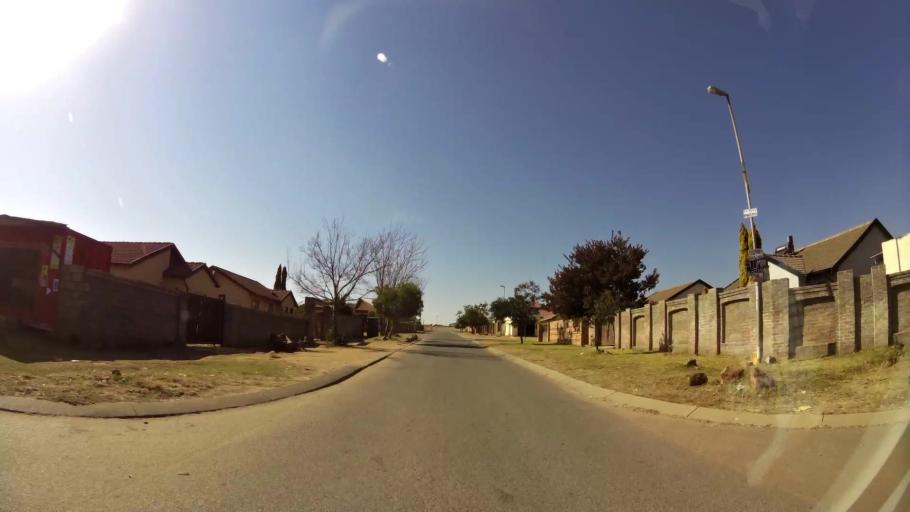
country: ZA
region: Gauteng
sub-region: Ekurhuleni Metropolitan Municipality
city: Tembisa
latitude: -26.0398
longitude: 28.1980
